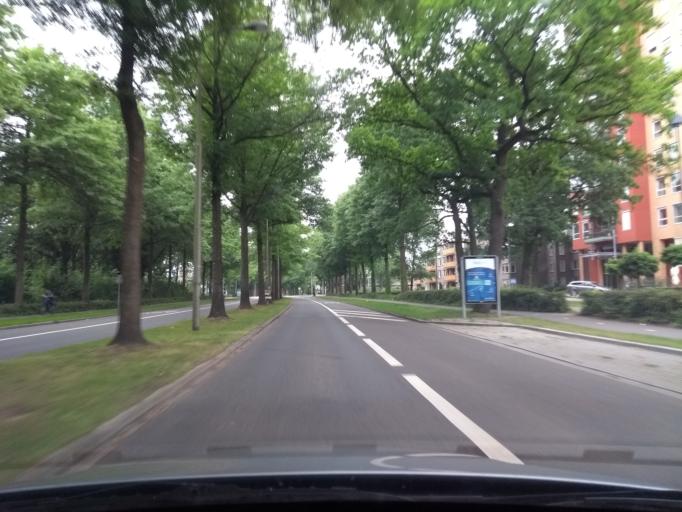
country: NL
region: Overijssel
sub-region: Gemeente Almelo
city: Almelo
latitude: 52.3710
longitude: 6.6783
